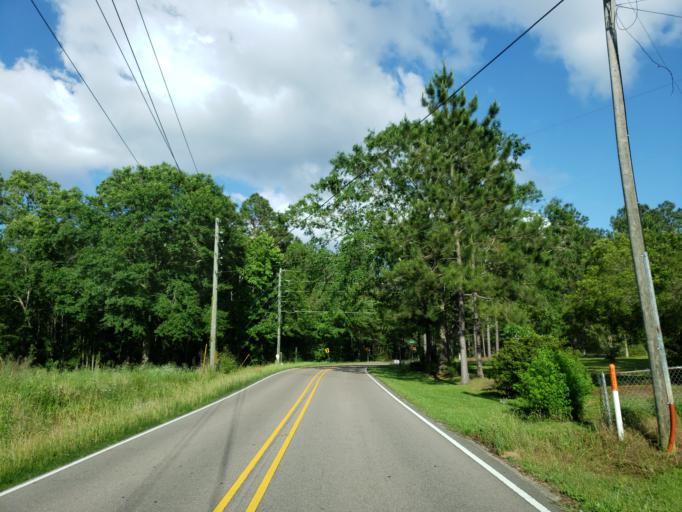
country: US
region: Mississippi
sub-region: Lamar County
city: West Hattiesburg
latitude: 31.2737
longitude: -89.3655
